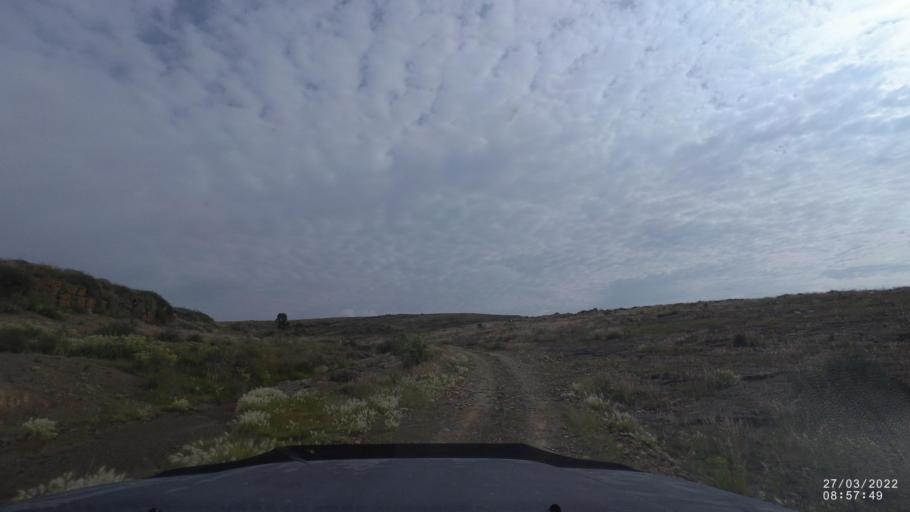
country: BO
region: Cochabamba
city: Cliza
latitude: -17.7453
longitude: -65.8576
